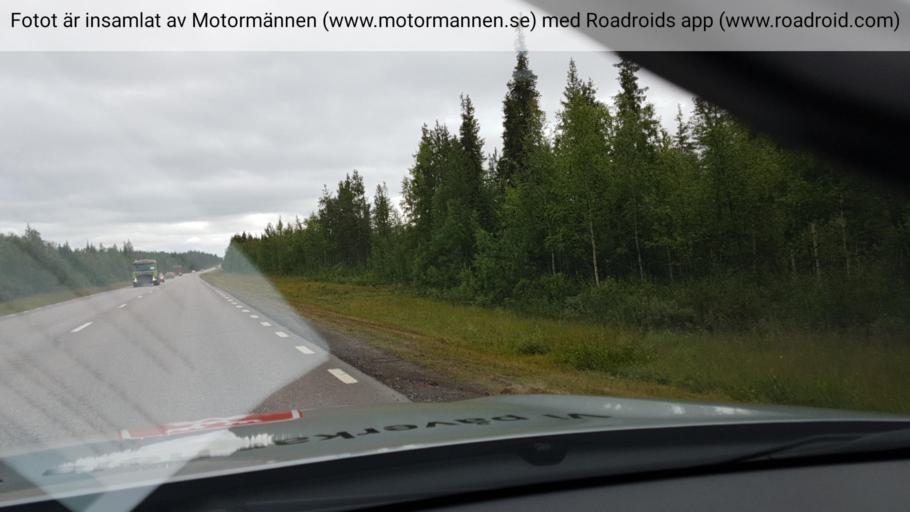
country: SE
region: Norrbotten
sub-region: Gallivare Kommun
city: Gaellivare
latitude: 67.0882
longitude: 21.0157
